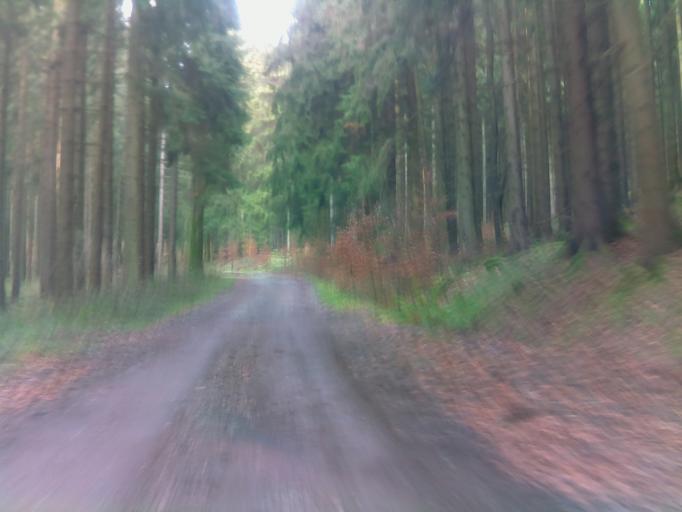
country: DE
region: Thuringia
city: Finsterbergen
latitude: 50.8295
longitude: 10.5624
